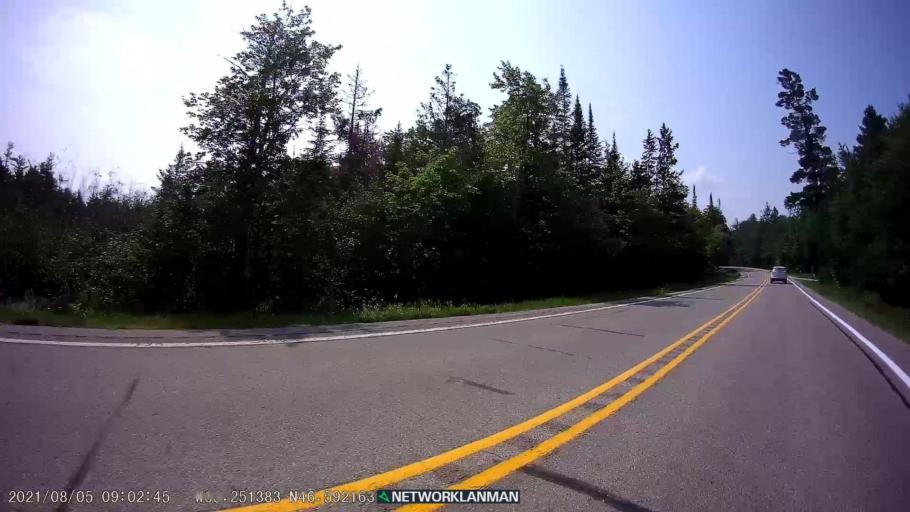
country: US
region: Michigan
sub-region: Luce County
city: Newberry
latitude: 46.5918
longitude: -85.2517
